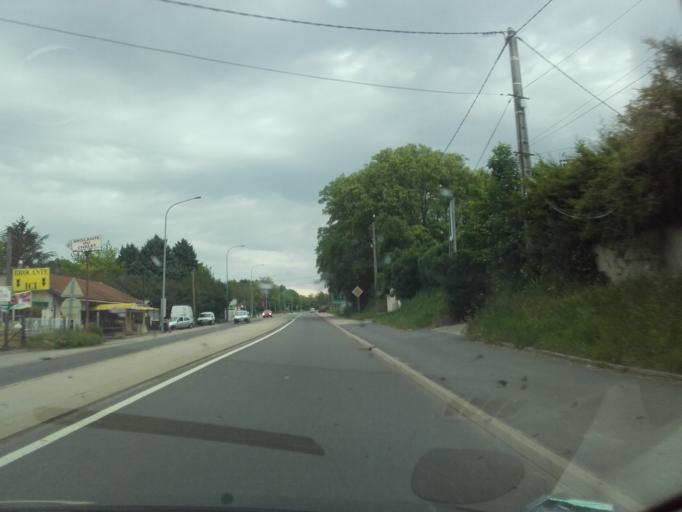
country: FR
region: Rhone-Alpes
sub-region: Departement du Rhone
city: Lissieu
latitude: 45.8461
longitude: 4.7334
